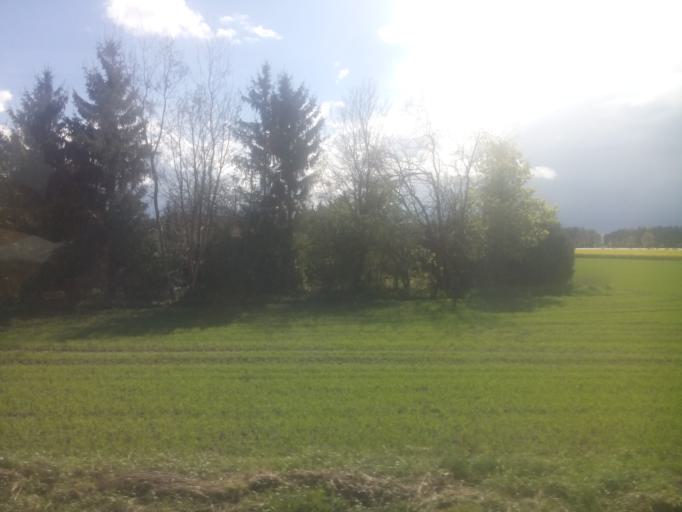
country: DE
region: Brandenburg
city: Kremmen
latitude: 52.7456
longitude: 13.0565
